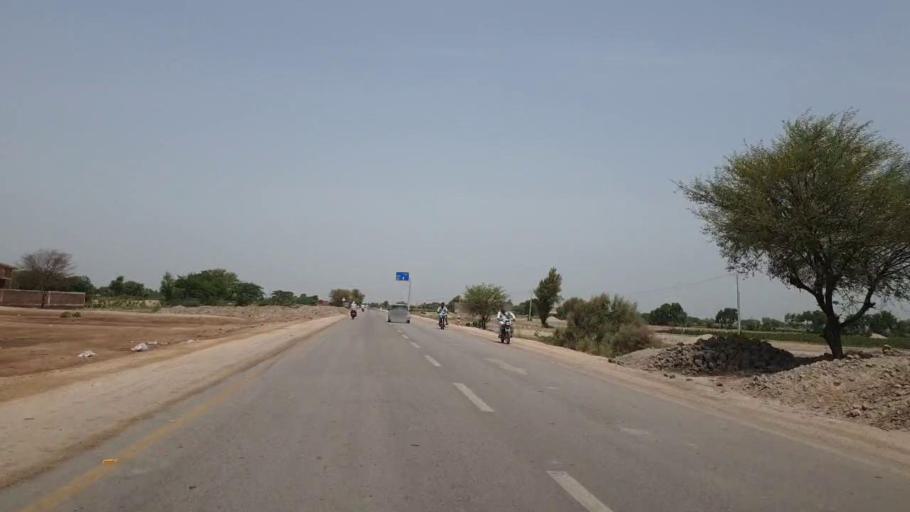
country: PK
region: Sindh
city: Shahpur Chakar
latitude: 26.1896
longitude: 68.5809
